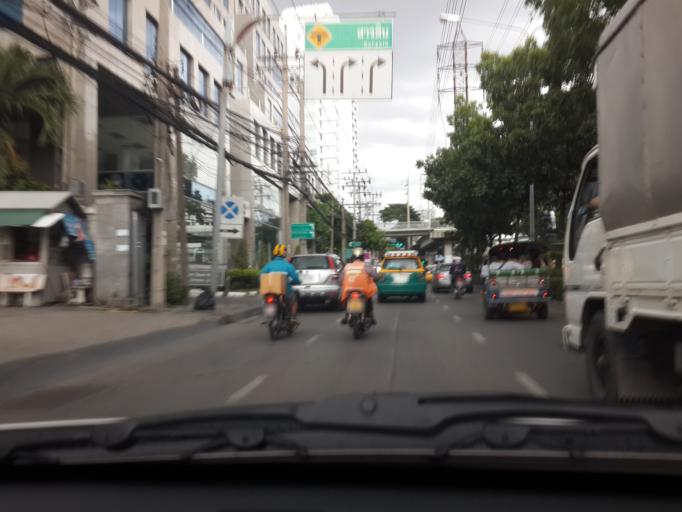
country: TH
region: Bangkok
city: Pathum Wan
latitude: 13.7342
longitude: 100.5448
